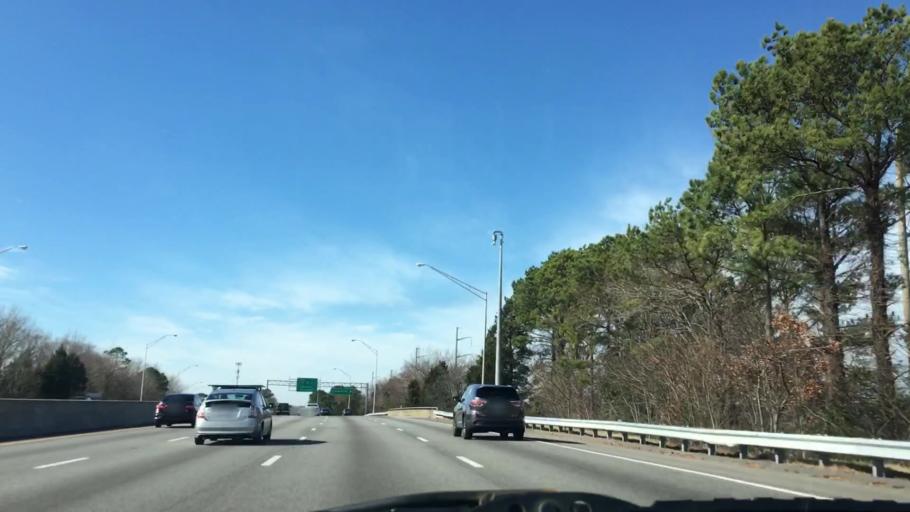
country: US
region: Virginia
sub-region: City of Virginia Beach
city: Virginia Beach
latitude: 36.8366
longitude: -76.0888
